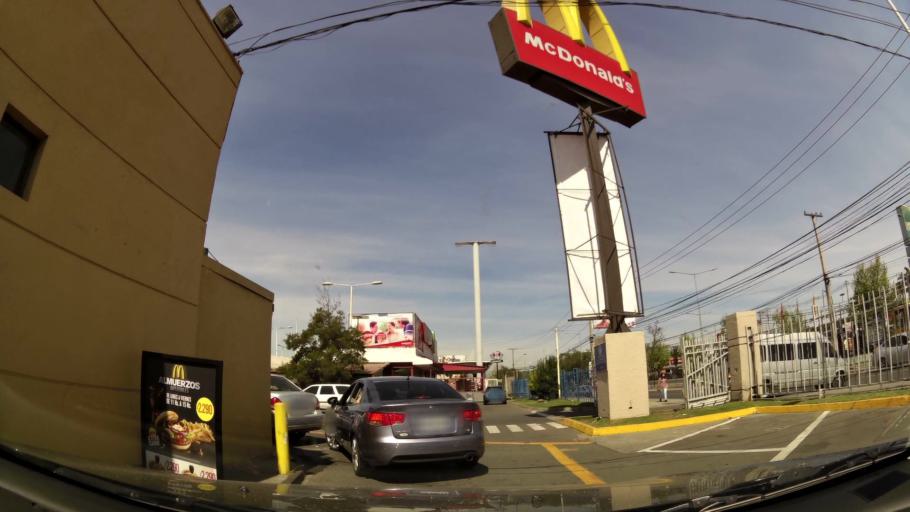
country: CL
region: Santiago Metropolitan
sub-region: Provincia de Cordillera
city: Puente Alto
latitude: -33.6006
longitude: -70.5772
